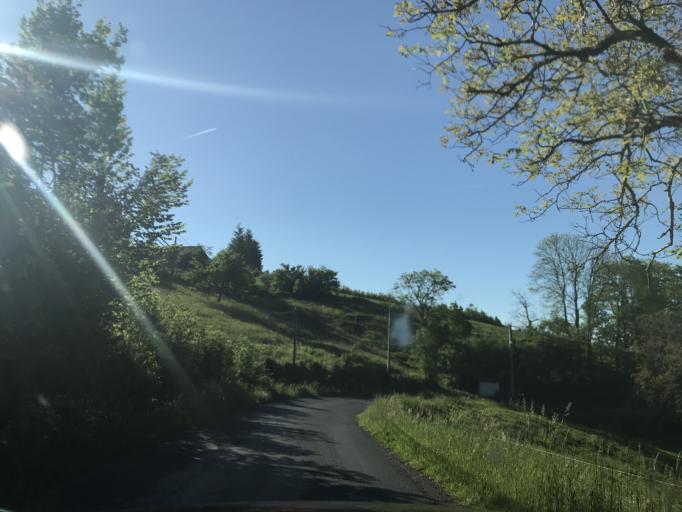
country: FR
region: Auvergne
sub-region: Departement du Puy-de-Dome
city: Job
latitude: 45.6745
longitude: 3.7010
